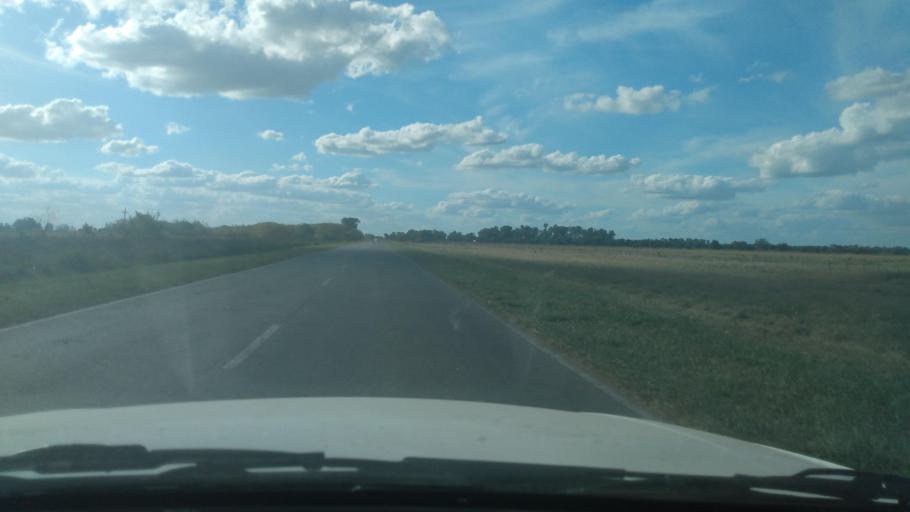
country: AR
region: Buenos Aires
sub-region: Partido de Navarro
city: Navarro
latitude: -34.9674
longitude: -59.3177
